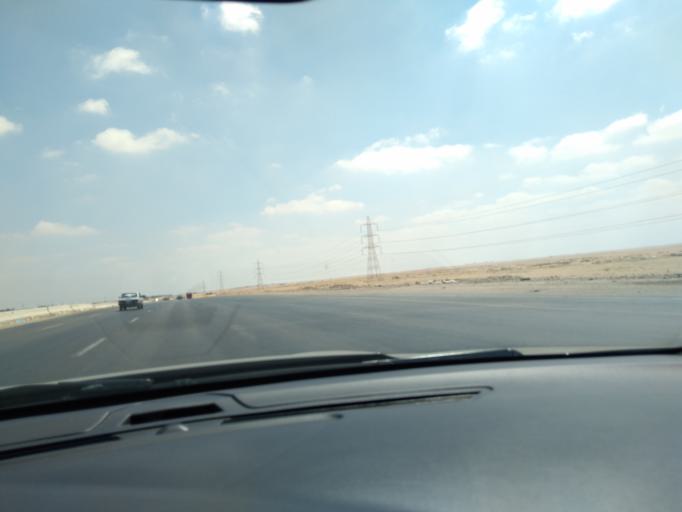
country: EG
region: Al Isma'iliyah
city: At Tall al Kabir
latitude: 30.3713
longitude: 31.9268
